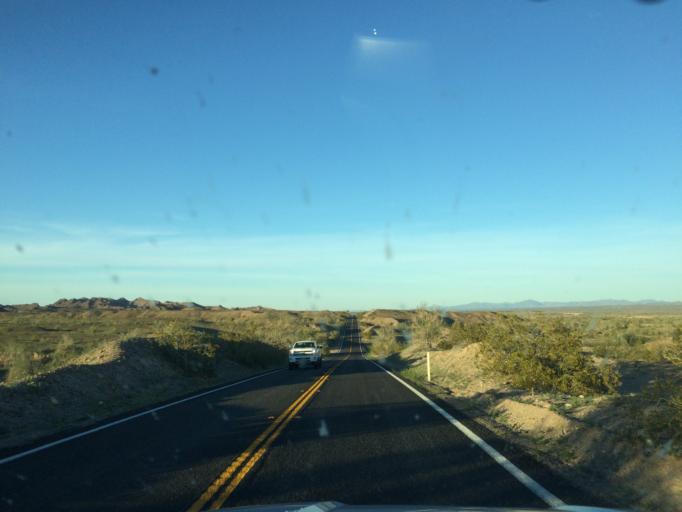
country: US
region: California
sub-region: Riverside County
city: Mesa Verde
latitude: 33.2963
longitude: -114.7501
